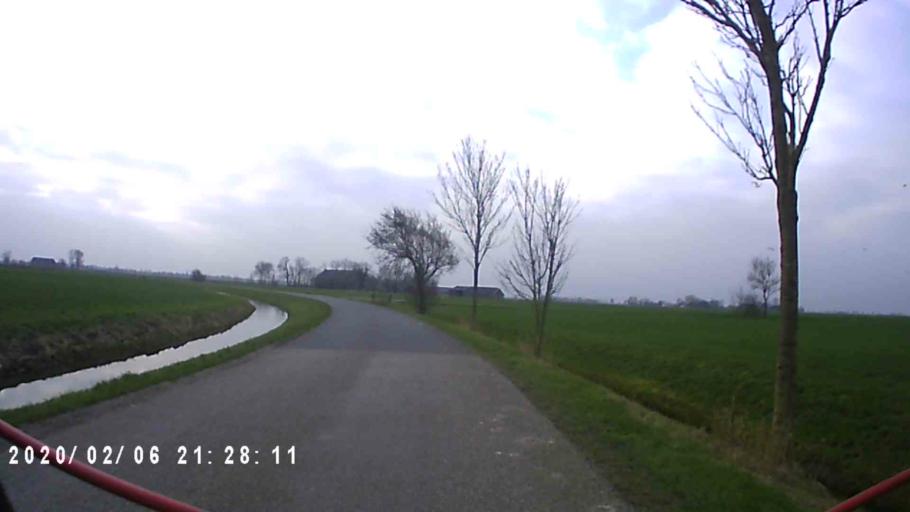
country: NL
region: Groningen
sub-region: Gemeente Zuidhorn
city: Noordhorn
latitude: 53.2821
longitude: 6.3783
